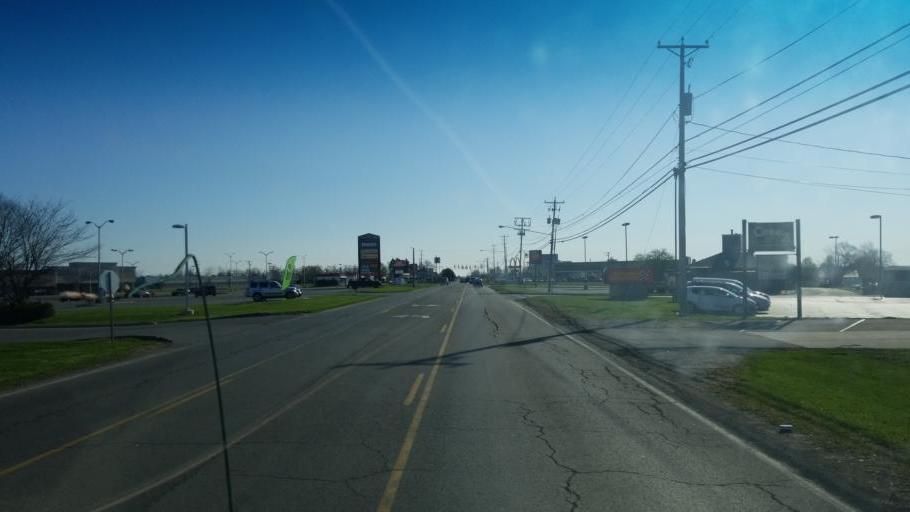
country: US
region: Ohio
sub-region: Hardin County
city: Kenton
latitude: 40.6512
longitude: -83.5930
